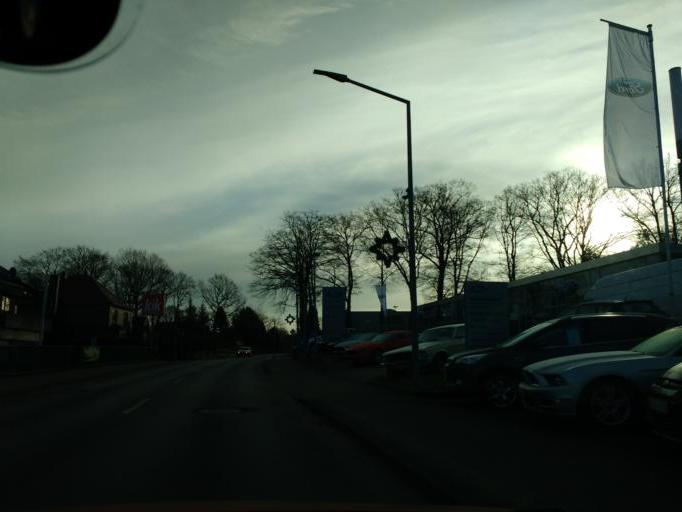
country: DE
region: Lower Saxony
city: Hude
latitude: 53.1082
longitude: 8.4686
